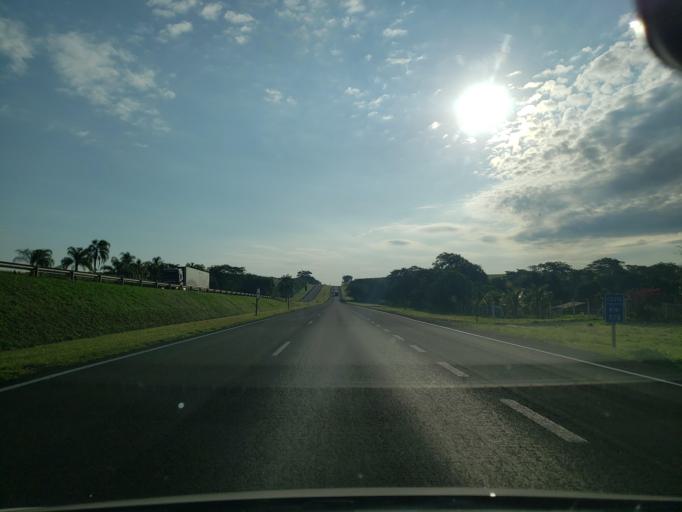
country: BR
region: Sao Paulo
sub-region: Valparaiso
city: Valparaiso
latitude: -21.2075
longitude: -50.8804
